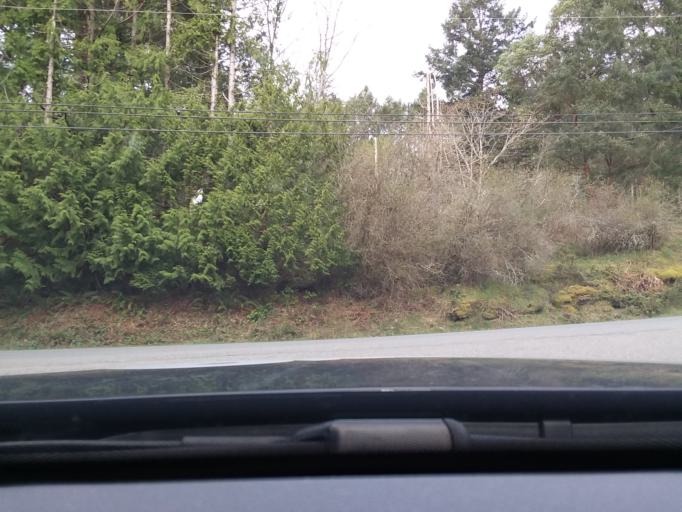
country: CA
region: British Columbia
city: North Saanich
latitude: 48.8750
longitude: -123.3205
